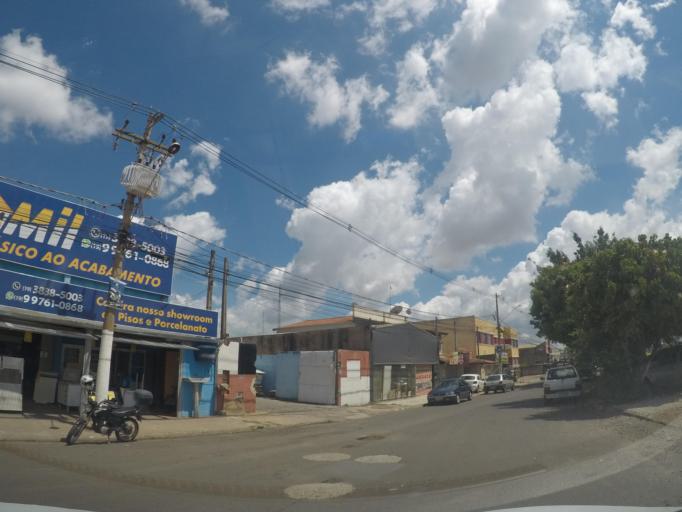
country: BR
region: Sao Paulo
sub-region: Hortolandia
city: Hortolandia
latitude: -22.8278
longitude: -47.2017
